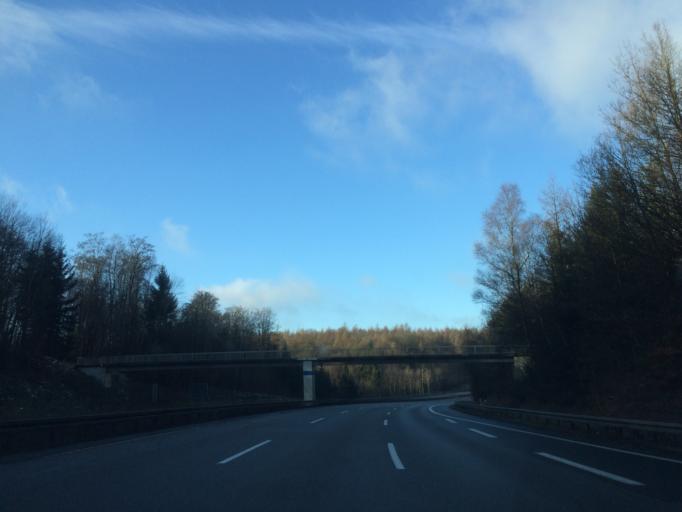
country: DE
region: Hesse
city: Schwarzenborn
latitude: 50.9447
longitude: 9.5266
